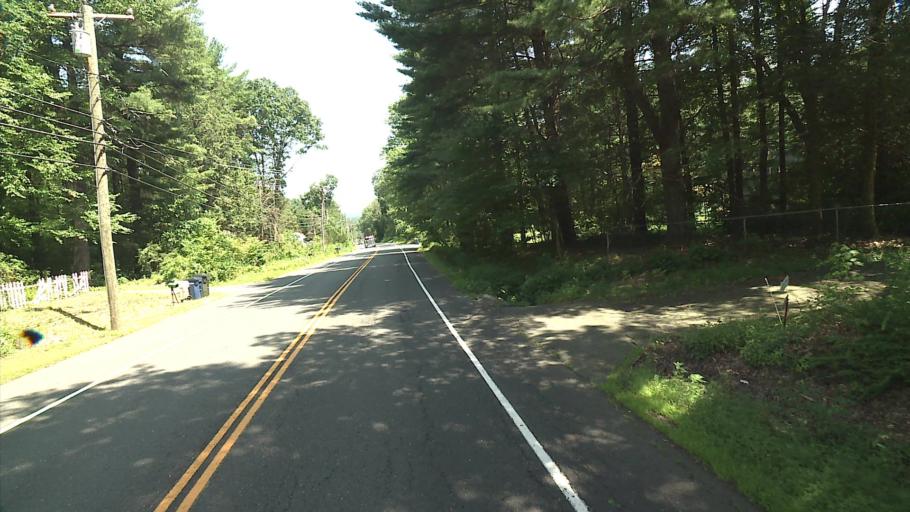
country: US
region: Connecticut
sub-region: Hartford County
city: Salmon Brook
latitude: 41.9552
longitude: -72.8241
